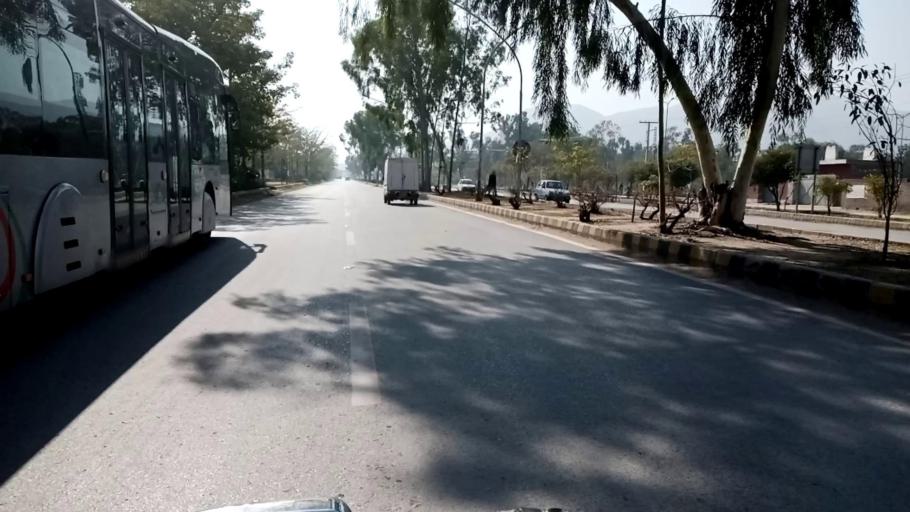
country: PK
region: Khyber Pakhtunkhwa
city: Peshawar
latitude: 33.9561
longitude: 71.4330
